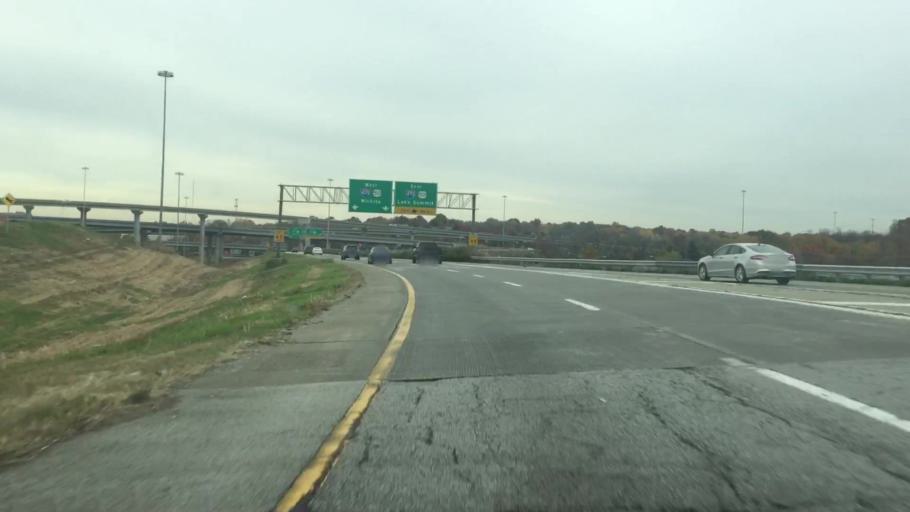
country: US
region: Missouri
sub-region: Jackson County
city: Grandview
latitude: 38.9278
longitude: -94.5267
